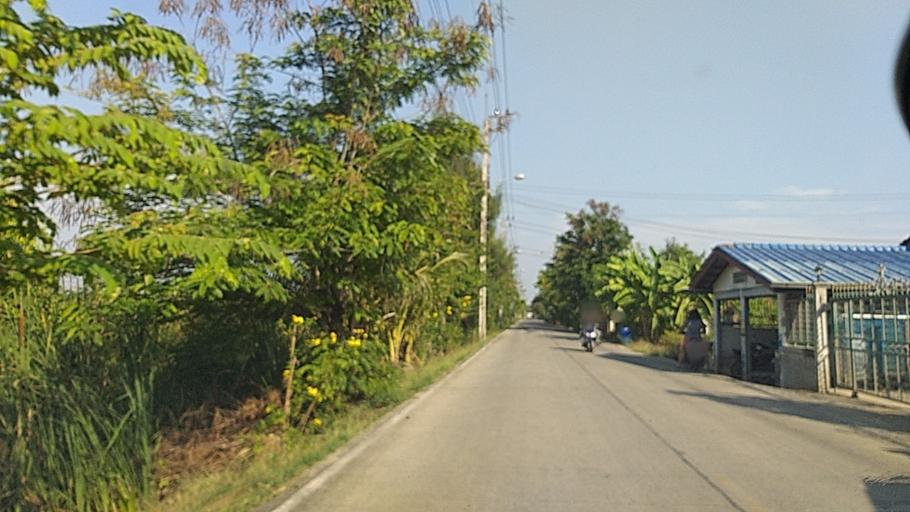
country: TH
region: Nonthaburi
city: Sai Noi
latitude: 13.9373
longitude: 100.3391
